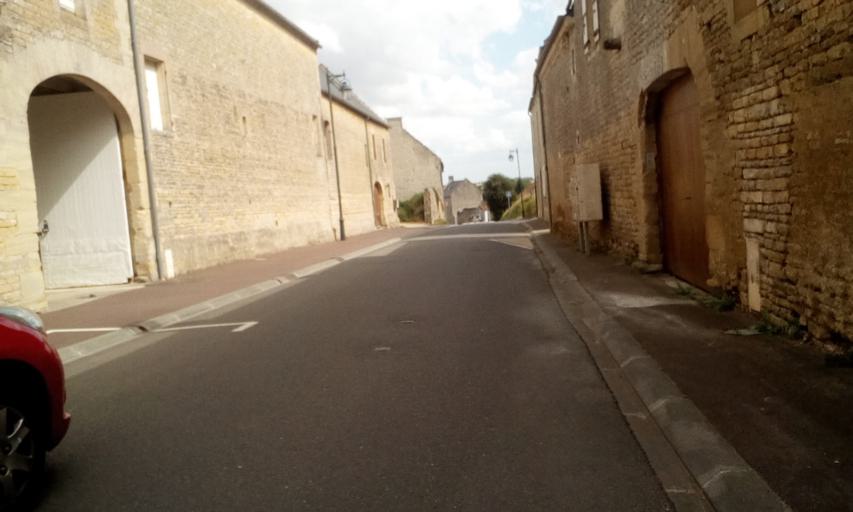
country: FR
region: Lower Normandy
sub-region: Departement du Calvados
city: Courseulles-sur-Mer
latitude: 49.3114
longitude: -0.4833
